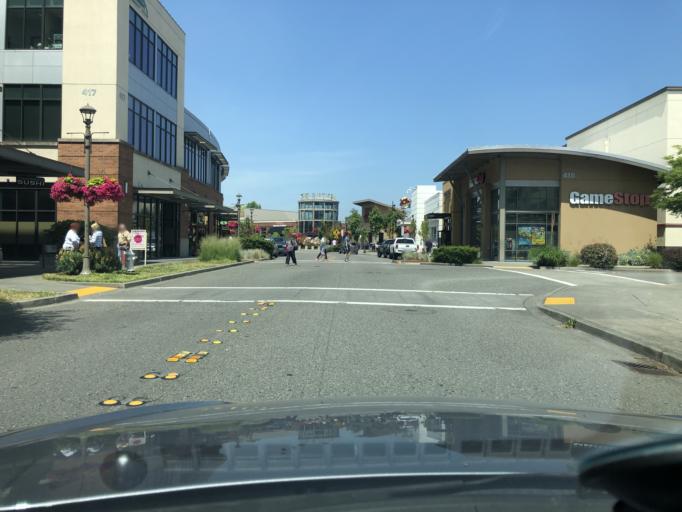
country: US
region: Washington
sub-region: King County
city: Kent
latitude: 47.3839
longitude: -122.2348
